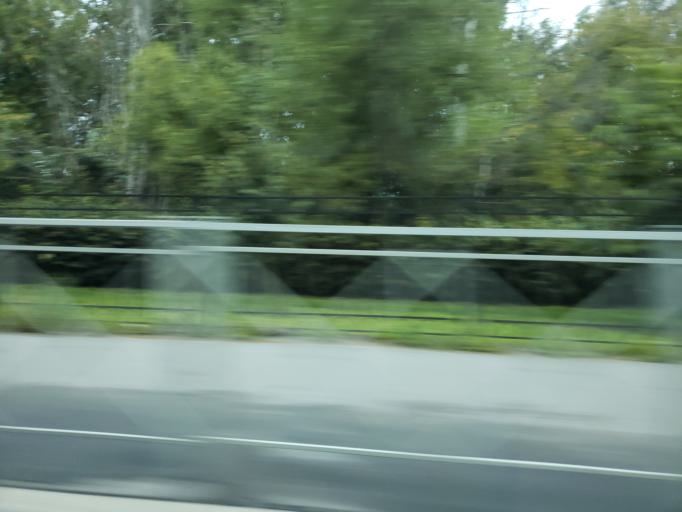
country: RU
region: St.-Petersburg
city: Vasyl'evsky Ostrov
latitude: 59.9407
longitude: 30.2522
